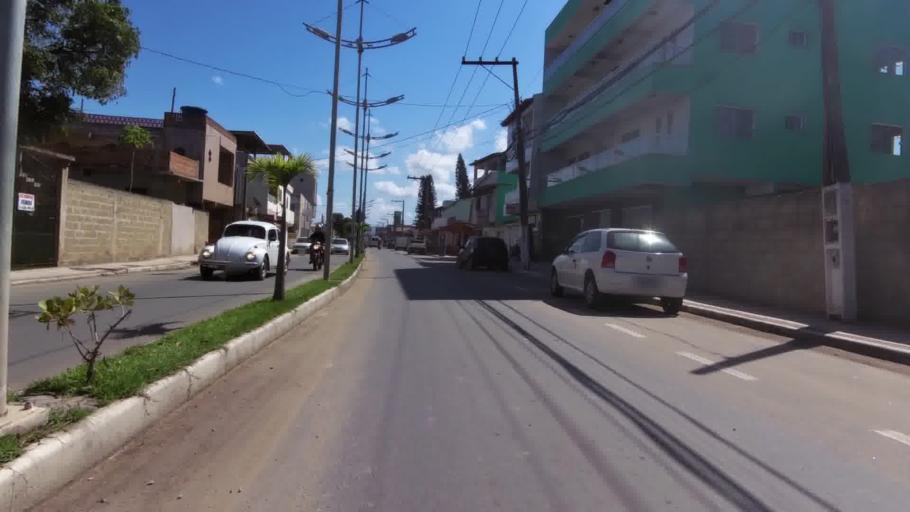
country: BR
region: Espirito Santo
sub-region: Piuma
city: Piuma
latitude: -20.8146
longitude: -40.6306
